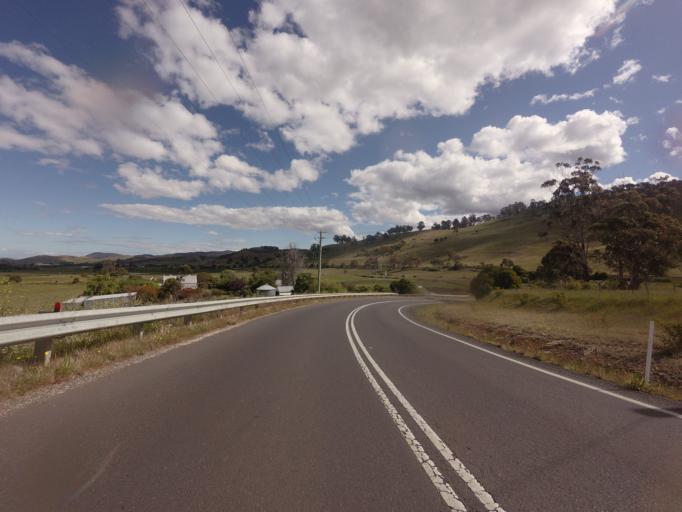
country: AU
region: Tasmania
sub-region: Brighton
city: Bridgewater
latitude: -42.5062
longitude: 147.3506
